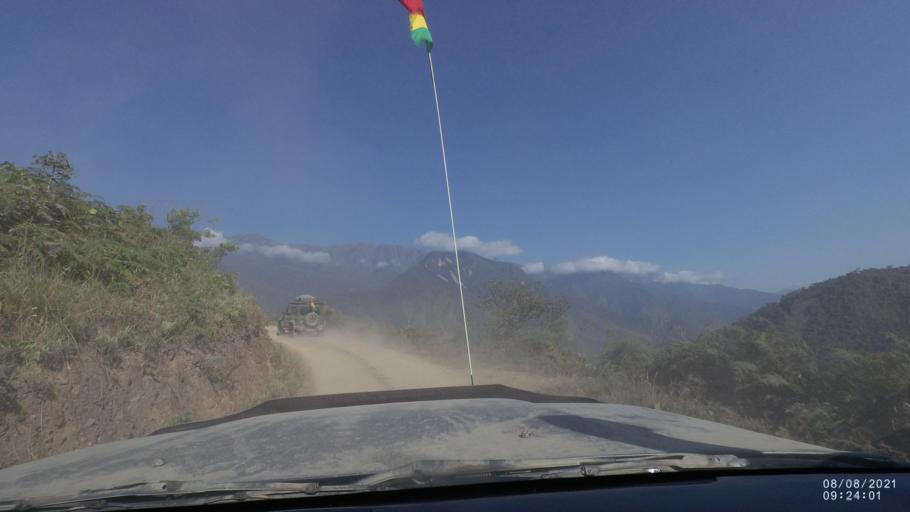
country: BO
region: La Paz
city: Quime
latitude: -16.5766
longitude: -66.7204
